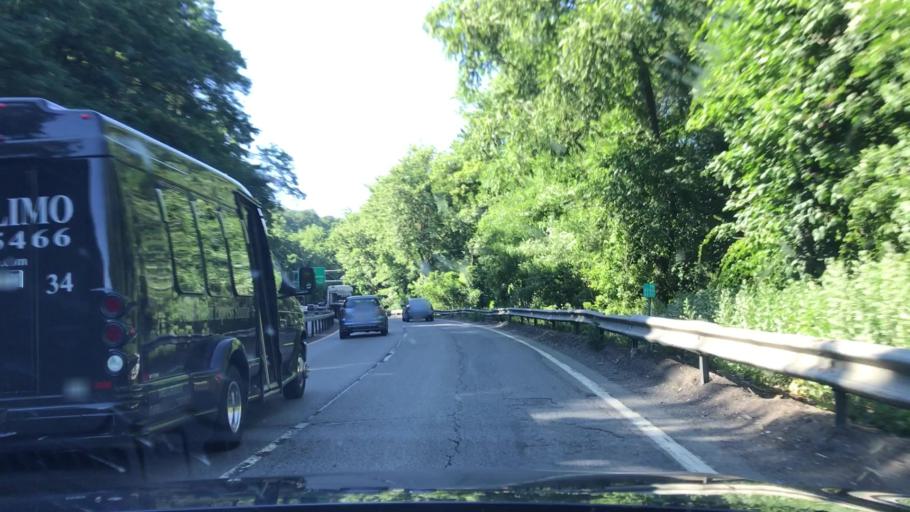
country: US
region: New York
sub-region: Westchester County
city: Hawthorne
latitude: 41.1122
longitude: -73.8053
